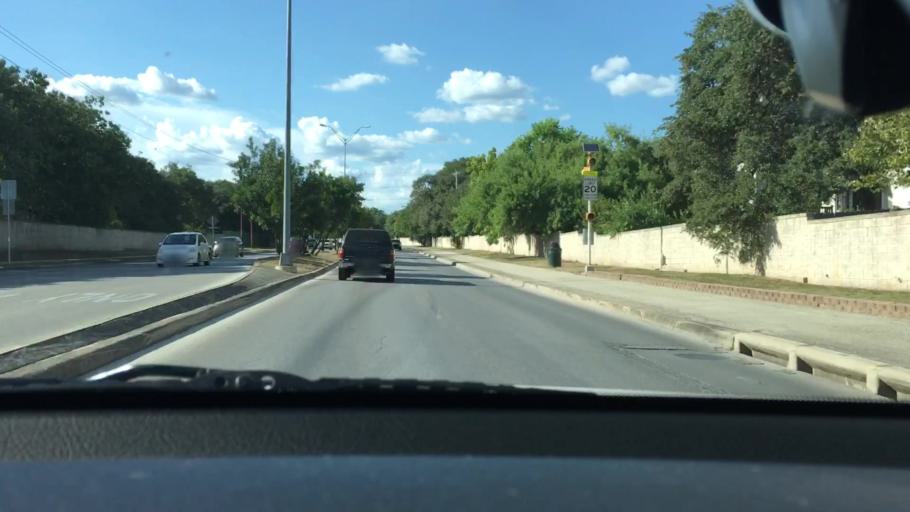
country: US
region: Texas
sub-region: Bexar County
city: Selma
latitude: 29.5787
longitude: -98.2807
